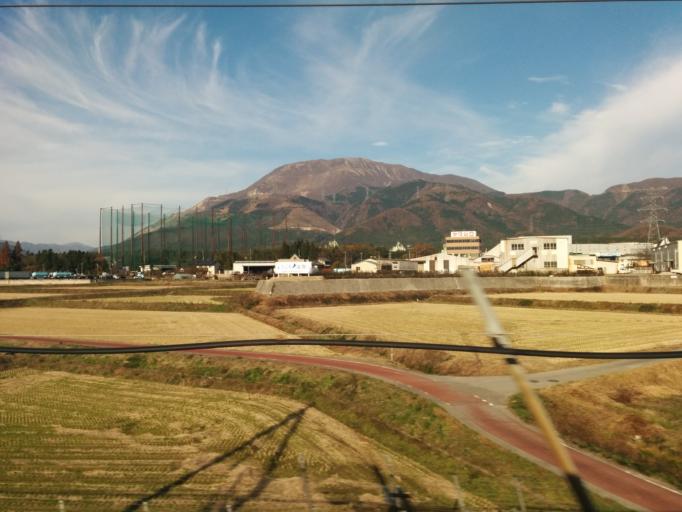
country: JP
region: Shiga Prefecture
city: Nagahama
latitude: 35.3636
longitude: 136.3919
